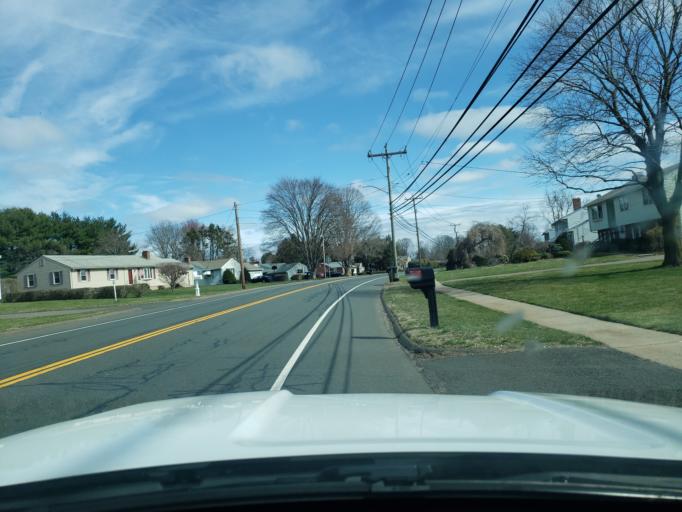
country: US
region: Connecticut
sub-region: Hartford County
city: Newington
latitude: 41.6629
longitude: -72.6786
